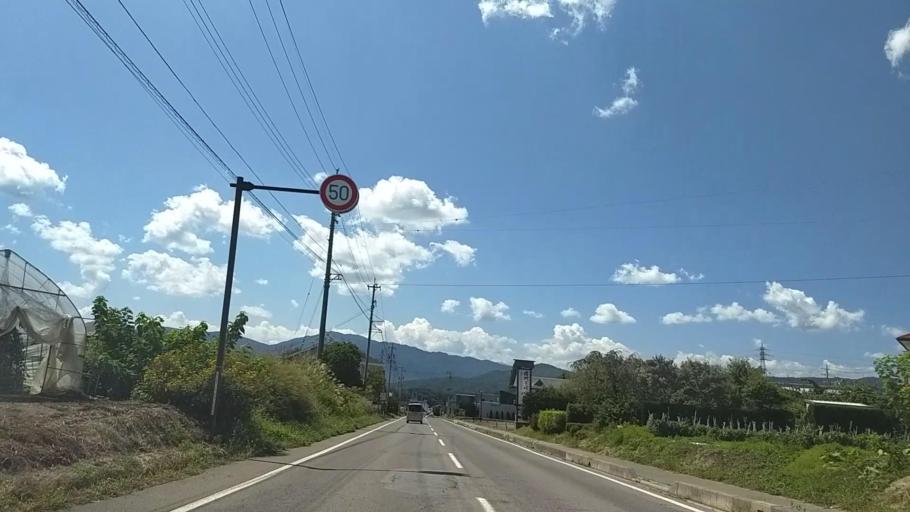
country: JP
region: Nagano
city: Chino
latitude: 36.0223
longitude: 138.2089
